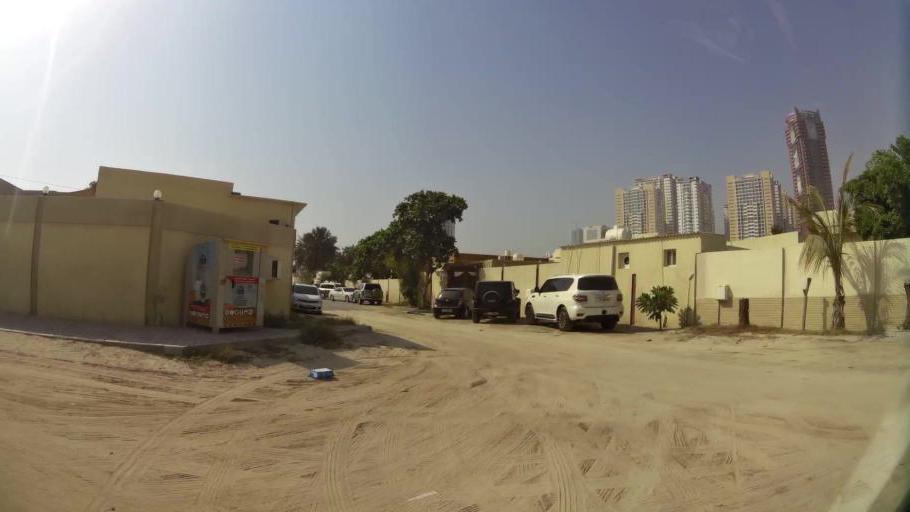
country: AE
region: Ajman
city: Ajman
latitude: 25.3902
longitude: 55.4284
